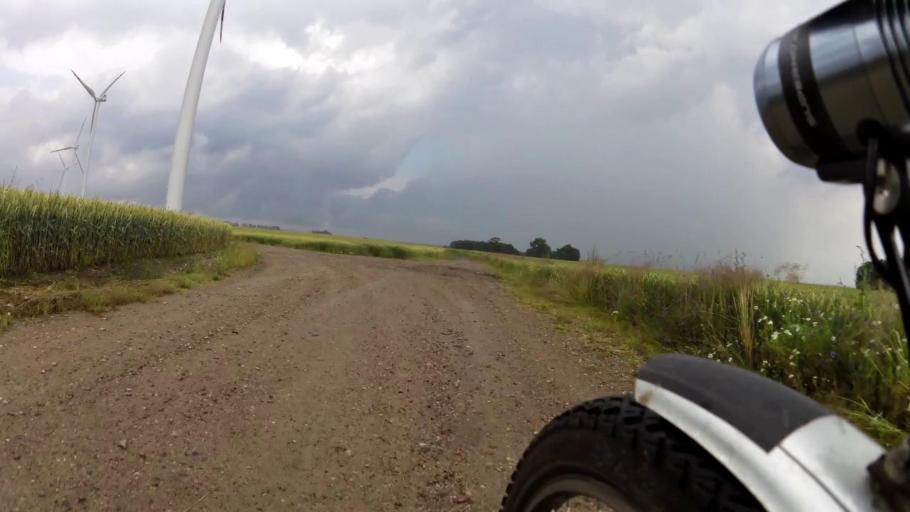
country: PL
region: West Pomeranian Voivodeship
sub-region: Powiat lobeski
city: Lobez
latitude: 53.7133
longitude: 15.6356
